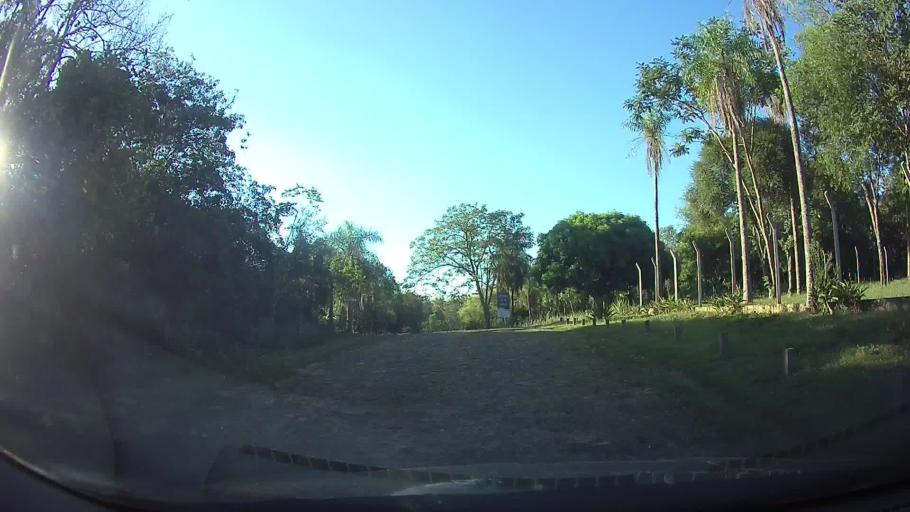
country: PY
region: Cordillera
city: San Bernardino
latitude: -25.3099
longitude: -57.2666
